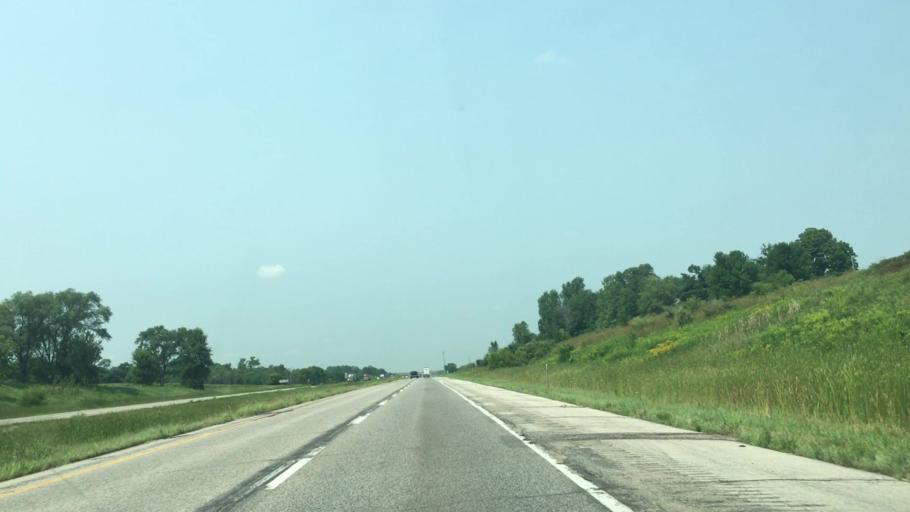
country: US
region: Iowa
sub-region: Benton County
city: Urbana
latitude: 42.2191
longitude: -91.8508
